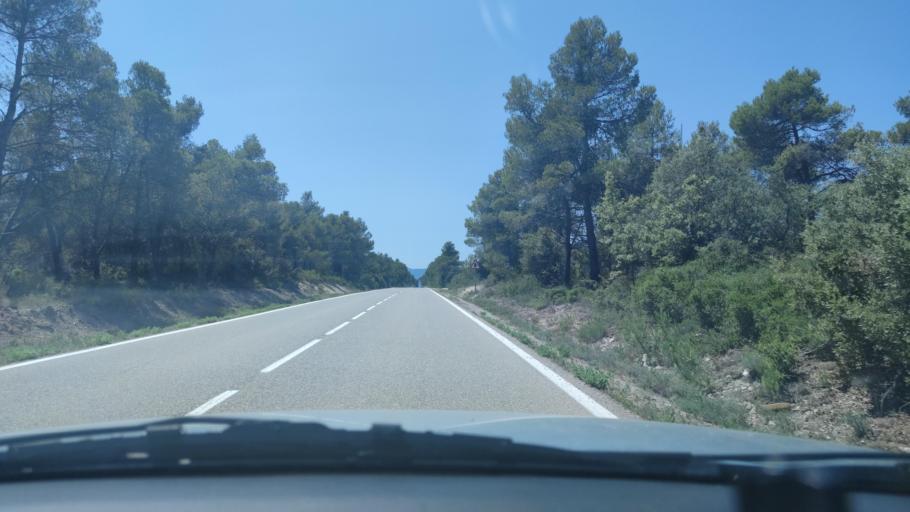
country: ES
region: Catalonia
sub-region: Provincia de Lleida
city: Fulleda
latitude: 41.4409
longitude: 1.0383
